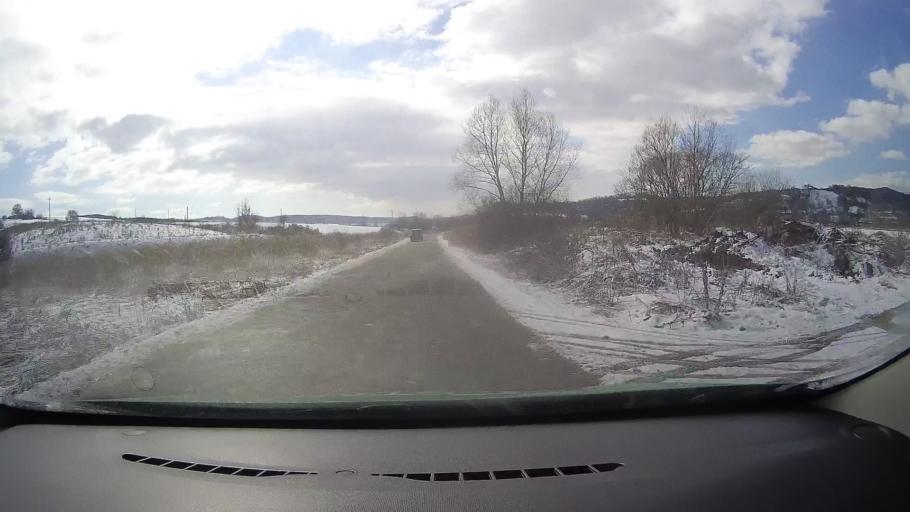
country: RO
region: Sibiu
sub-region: Comuna Mihaileni
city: Mihaileni
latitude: 46.0069
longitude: 24.3647
